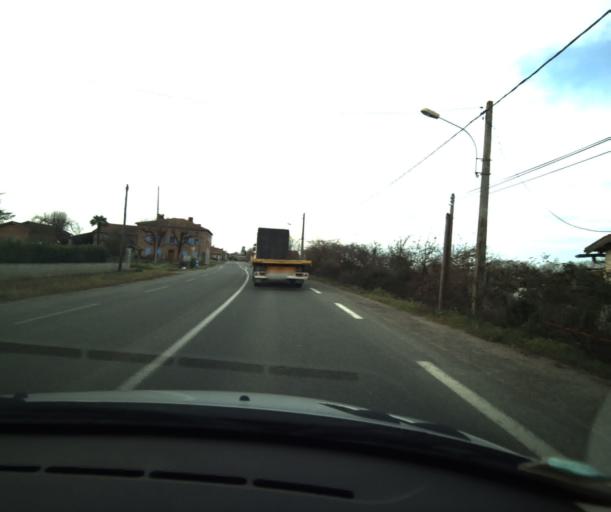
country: FR
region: Midi-Pyrenees
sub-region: Departement du Tarn-et-Garonne
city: Saint-Porquier
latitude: 44.0081
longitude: 1.1759
